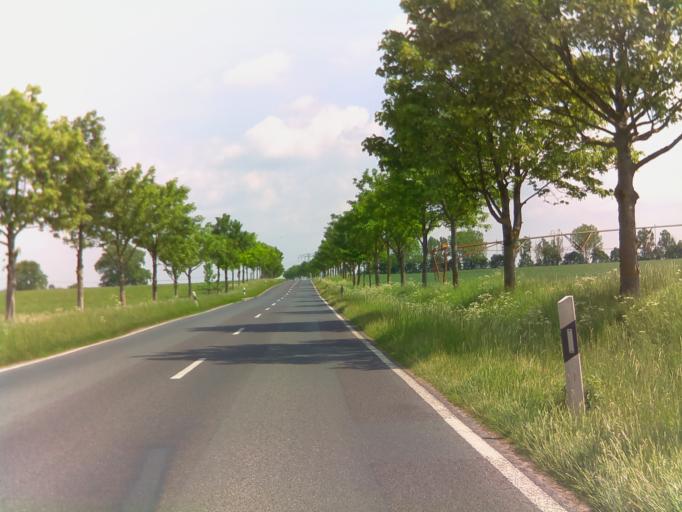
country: DE
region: Brandenburg
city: Retzow
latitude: 52.6123
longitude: 12.6595
